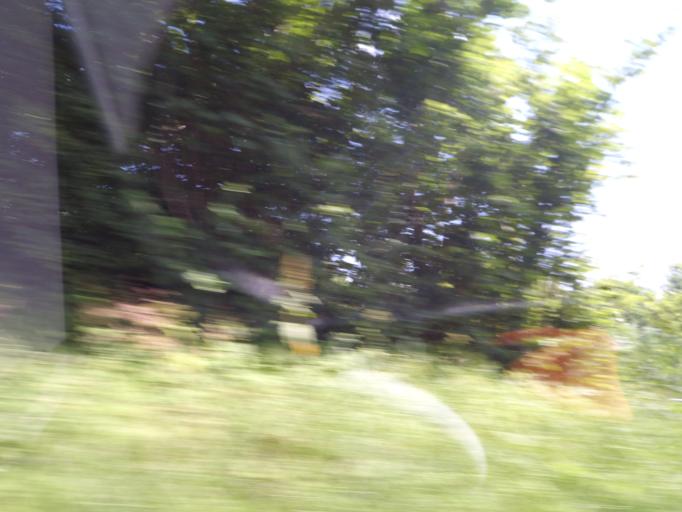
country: DK
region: South Denmark
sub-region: Assens Kommune
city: Arup
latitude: 55.3850
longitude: 10.0507
